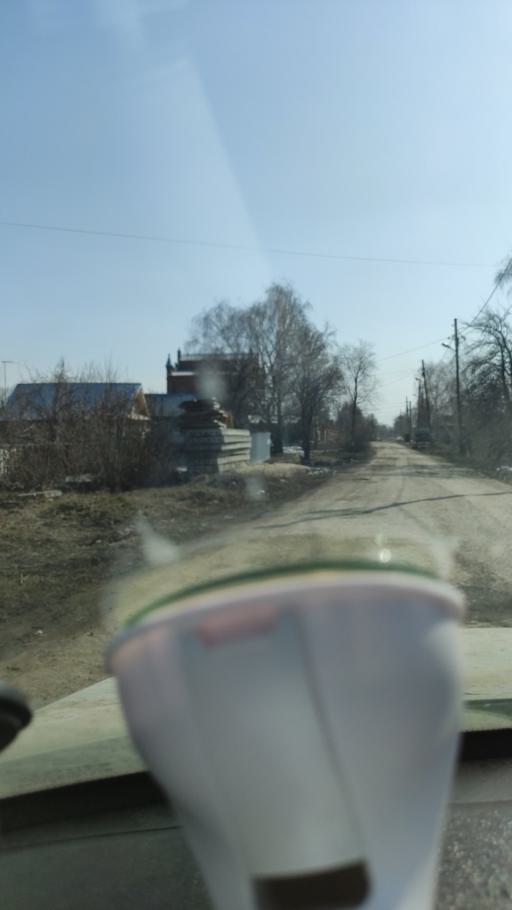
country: RU
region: Samara
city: Petra-Dubrava
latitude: 53.2547
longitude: 50.3486
